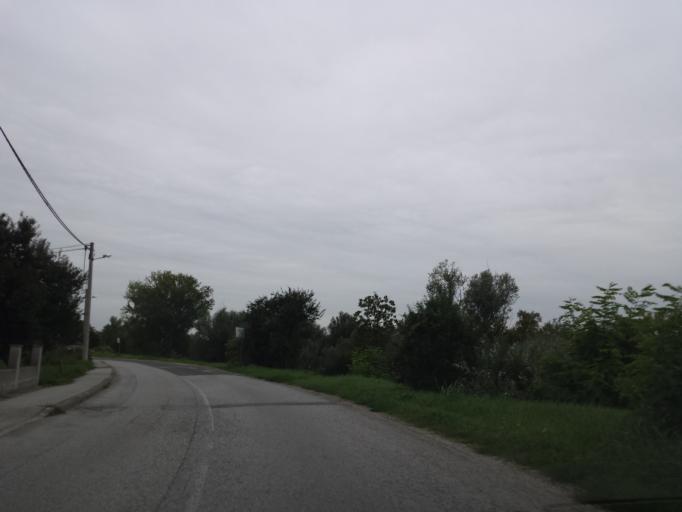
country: HR
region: Grad Zagreb
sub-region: Sesvete
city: Sesvete
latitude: 45.7941
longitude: 16.1206
